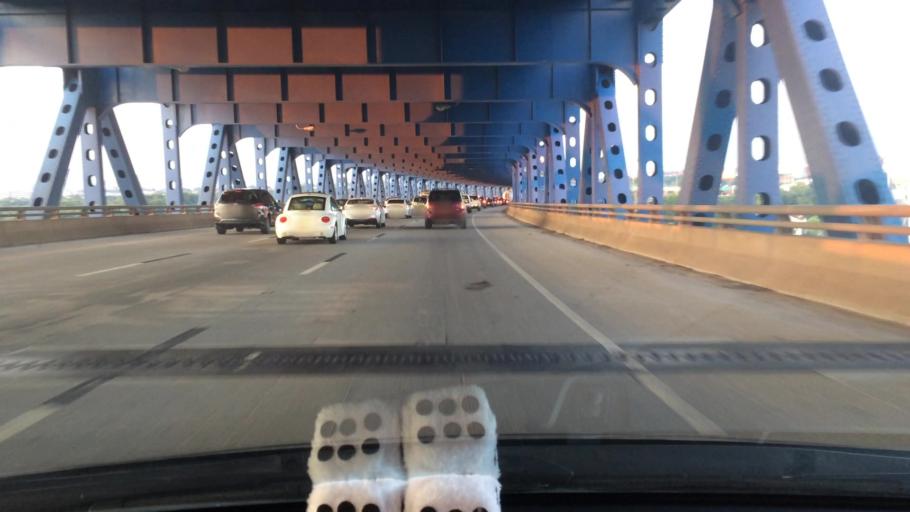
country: US
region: New Jersey
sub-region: Gloucester County
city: National Park
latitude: 39.8942
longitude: -75.1934
